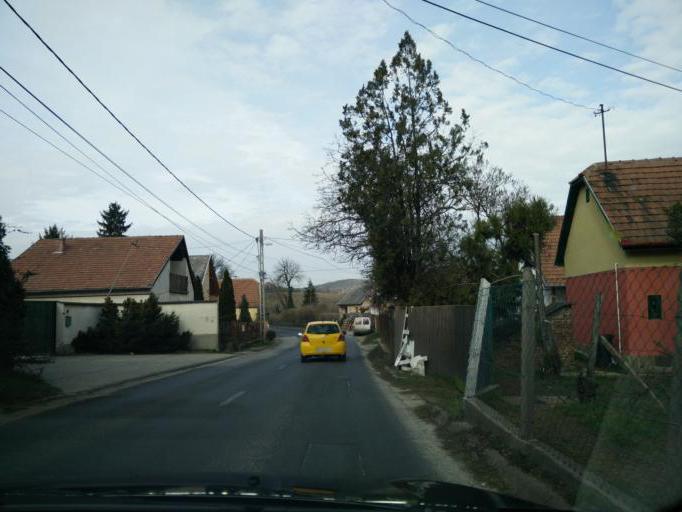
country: HU
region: Pest
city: Piliscsaba
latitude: 47.6300
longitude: 18.8200
